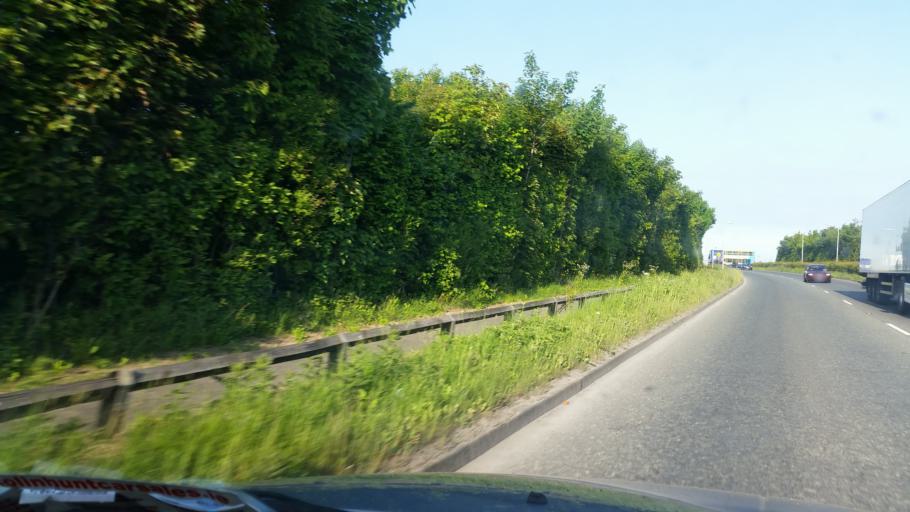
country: IE
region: Leinster
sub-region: Dublin City
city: Finglas
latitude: 53.4246
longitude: -6.3086
